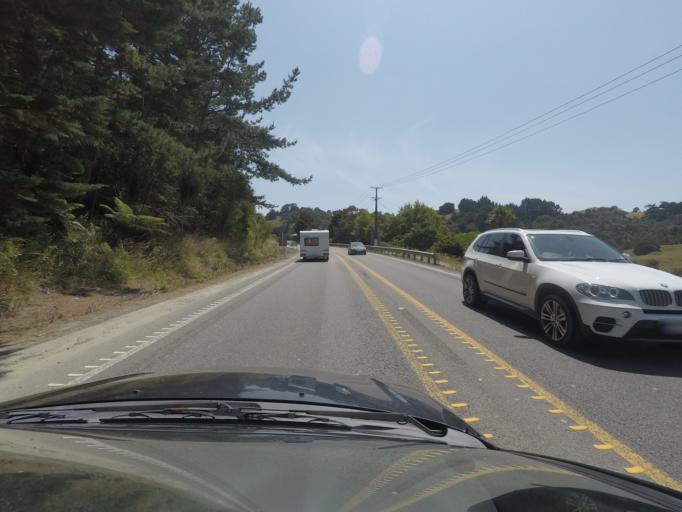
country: NZ
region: Auckland
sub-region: Auckland
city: Warkworth
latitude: -36.5127
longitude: 174.6703
